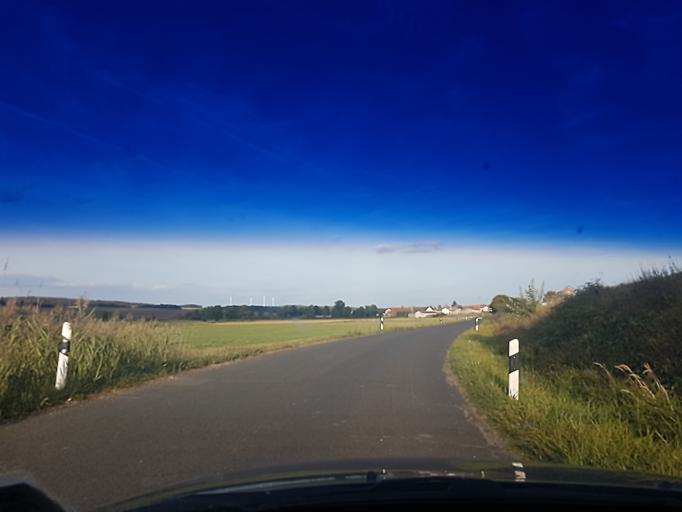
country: DE
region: Bavaria
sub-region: Regierungsbezirk Mittelfranken
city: Wachenroth
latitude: 49.7434
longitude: 10.6812
